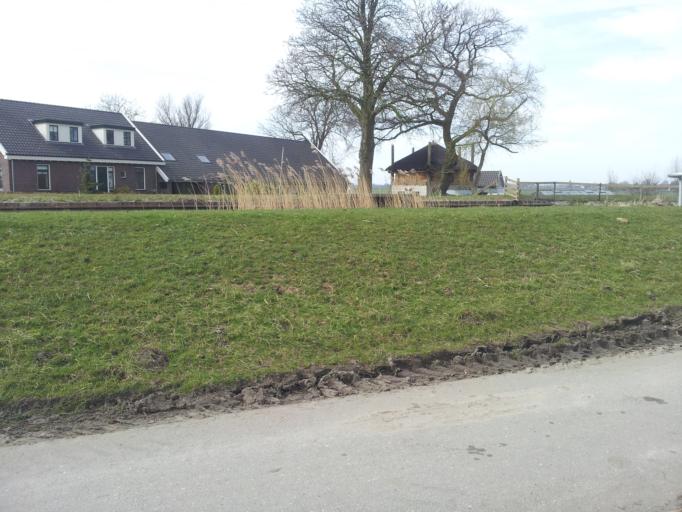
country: NL
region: South Holland
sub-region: Gemeente Zoetermeer
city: Zoetermeer
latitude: 52.0912
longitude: 4.5001
